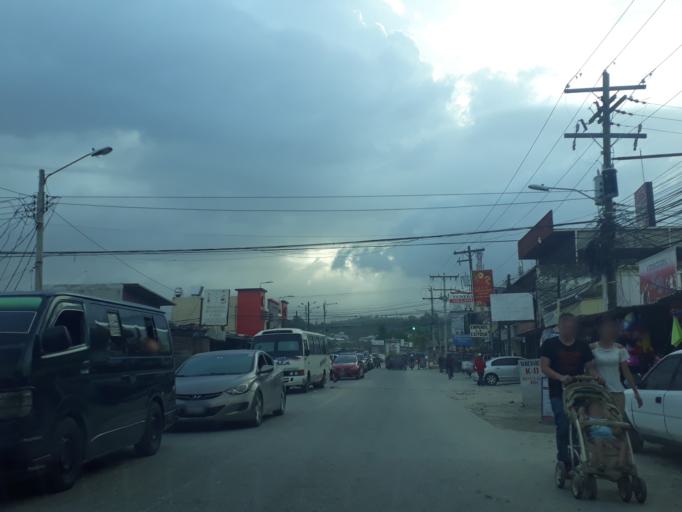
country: HN
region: Cortes
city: Choloma
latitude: 15.5731
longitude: -87.9527
